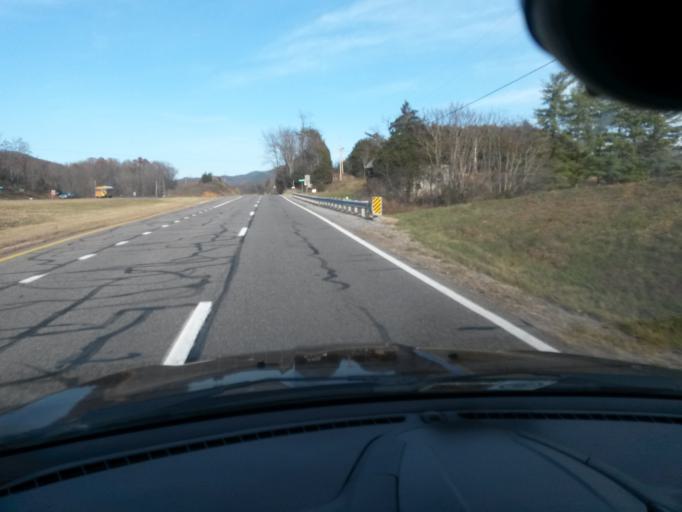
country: US
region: Virginia
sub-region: Botetourt County
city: Fincastle
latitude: 37.6181
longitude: -79.8259
